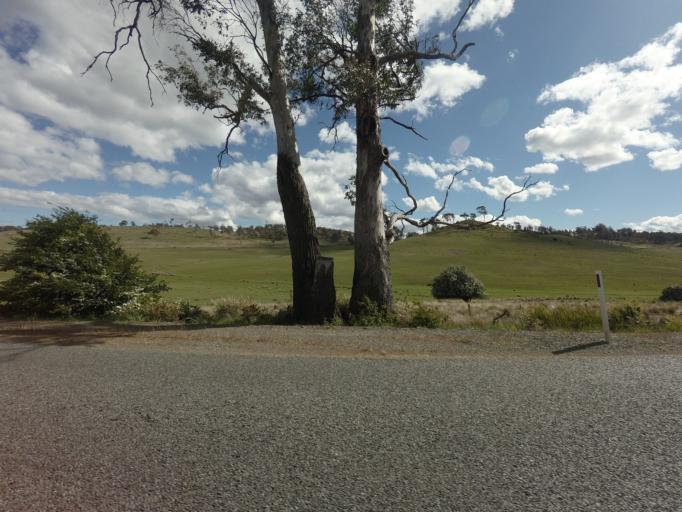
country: AU
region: Tasmania
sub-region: Brighton
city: Bridgewater
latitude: -42.4864
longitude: 147.3300
